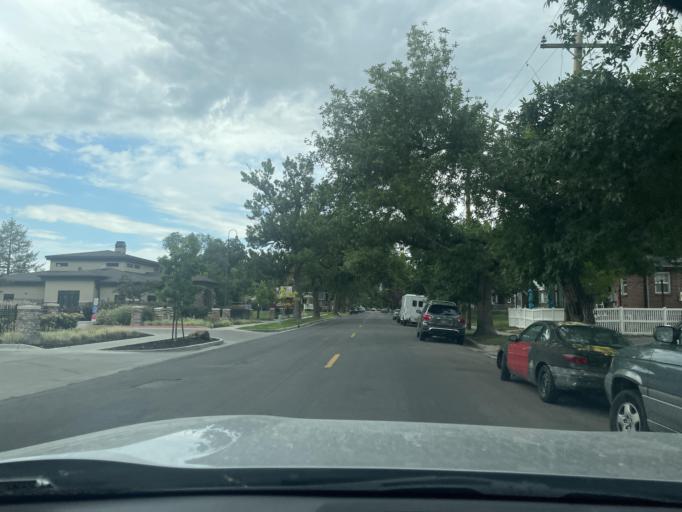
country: US
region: Utah
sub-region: Salt Lake County
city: South Salt Lake
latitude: 40.7308
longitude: -111.8940
